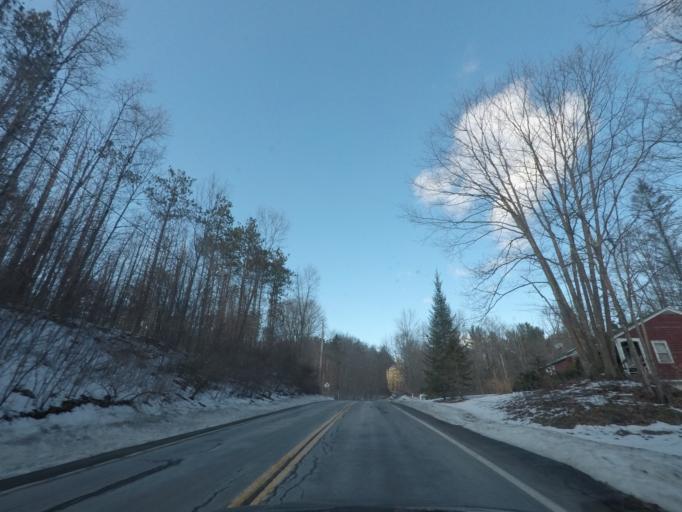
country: US
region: Massachusetts
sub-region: Berkshire County
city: West Stockbridge
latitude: 42.3172
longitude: -73.4715
